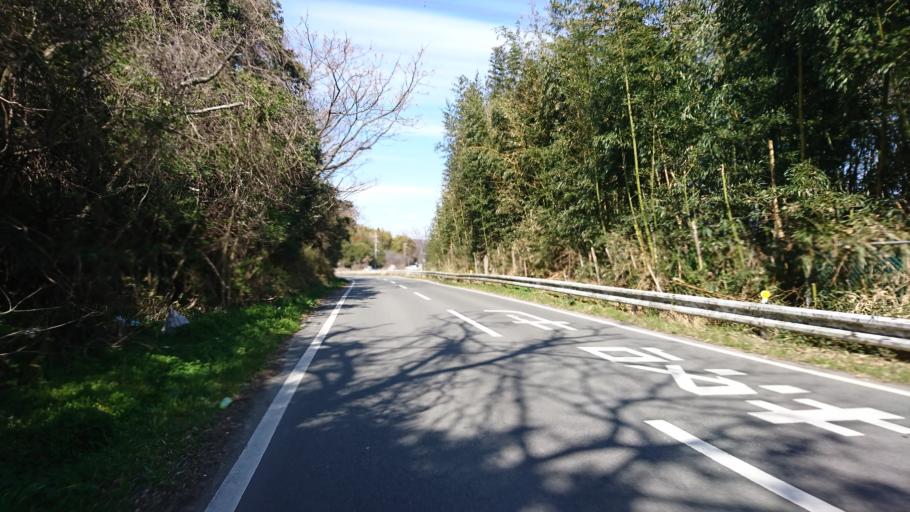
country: JP
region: Hyogo
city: Kakogawacho-honmachi
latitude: 34.8003
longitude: 134.8112
